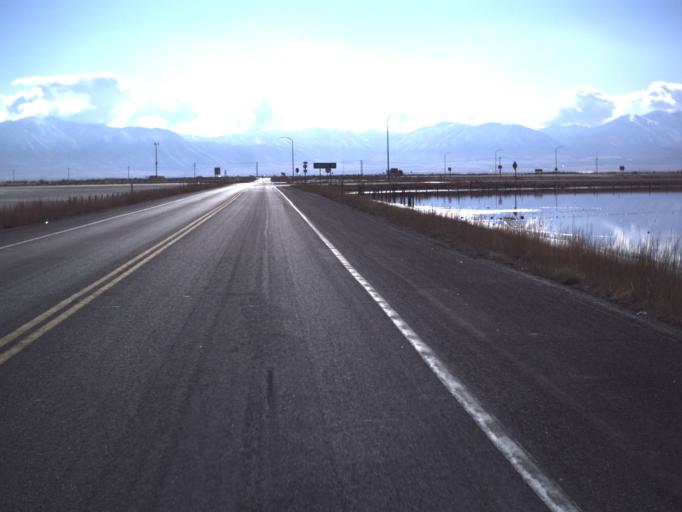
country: US
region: Utah
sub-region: Tooele County
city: Grantsville
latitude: 40.7104
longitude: -112.5254
